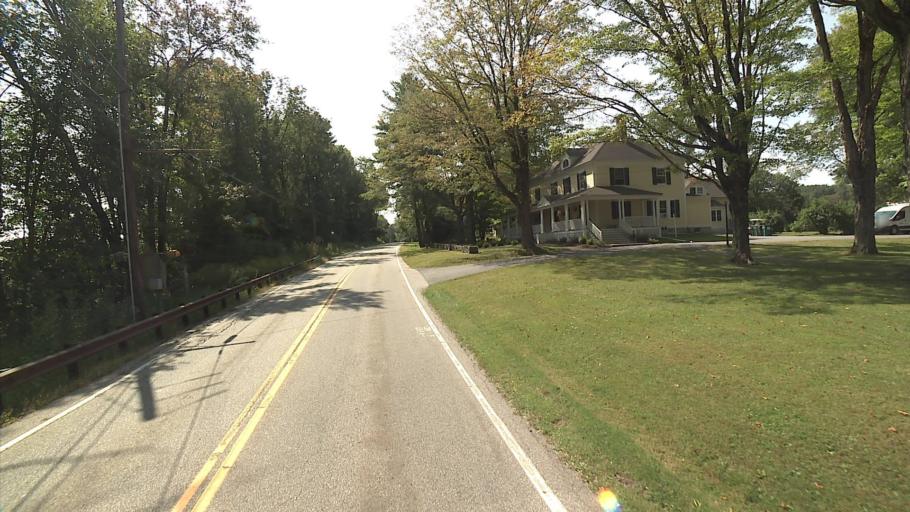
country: US
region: Connecticut
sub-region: Windham County
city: South Woodstock
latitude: 41.9255
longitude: -71.9567
